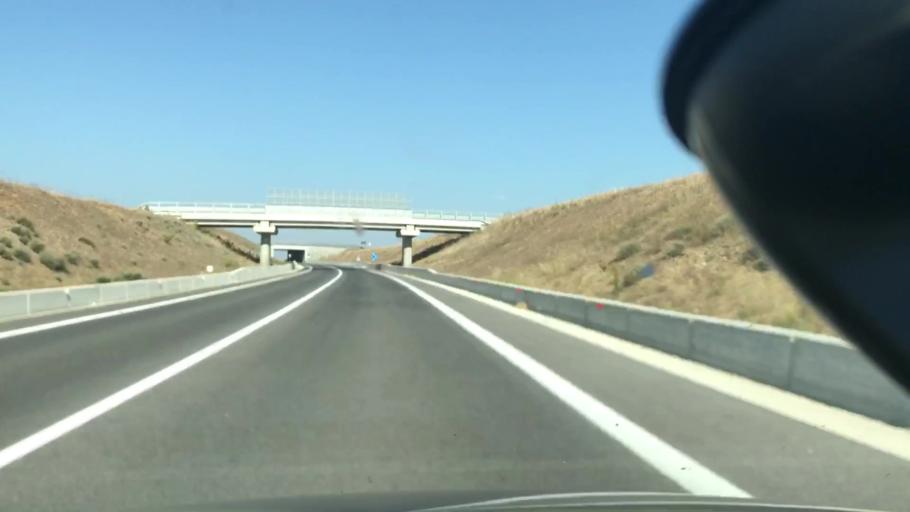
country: IT
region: Basilicate
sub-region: Provincia di Potenza
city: Palazzo San Gervasio
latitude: 40.9674
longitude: 16.0061
